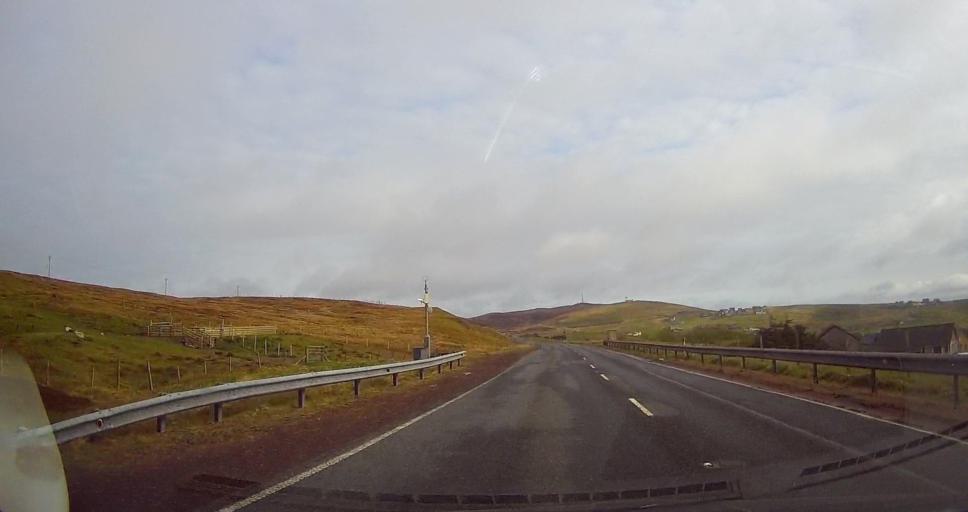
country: GB
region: Scotland
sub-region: Shetland Islands
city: Lerwick
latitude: 60.1265
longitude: -1.2165
